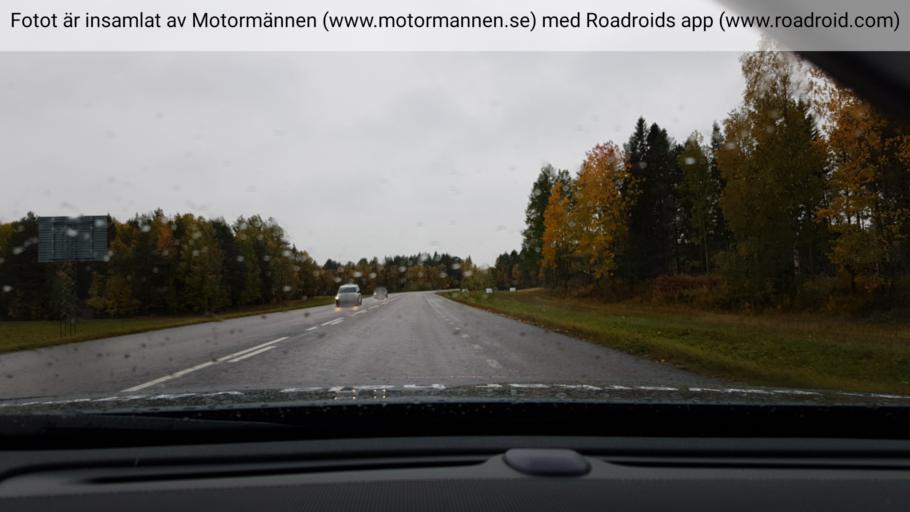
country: SE
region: Norrbotten
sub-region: Lulea Kommun
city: Gammelstad
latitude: 65.5860
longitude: 22.0261
